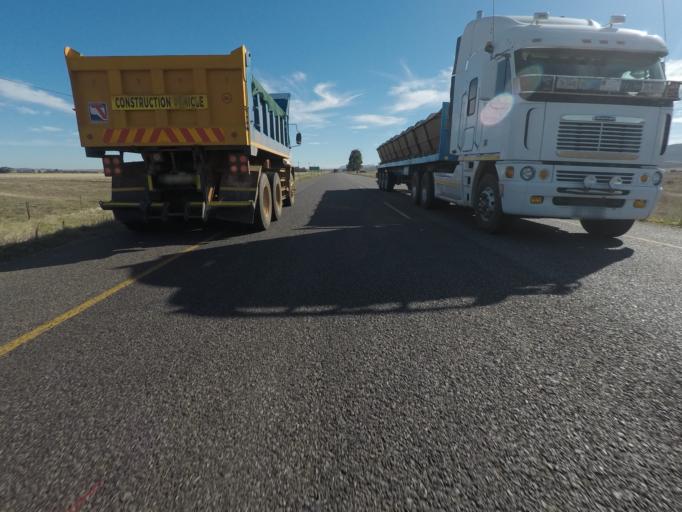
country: ZA
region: Western Cape
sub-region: West Coast District Municipality
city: Malmesbury
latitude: -33.6250
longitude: 18.7244
